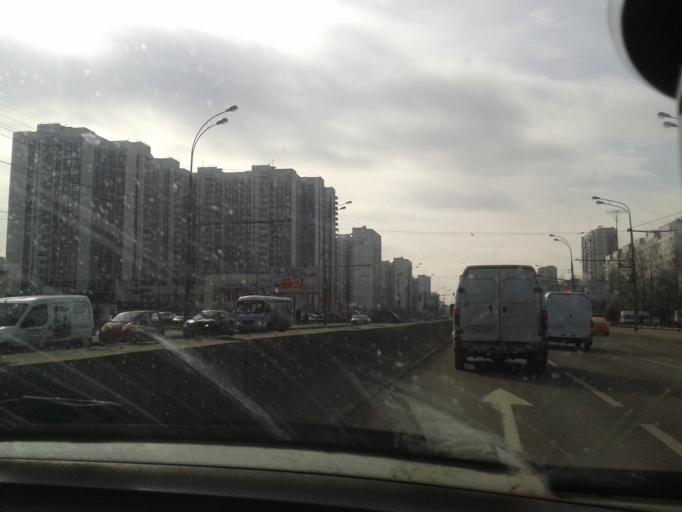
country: RU
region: Moscow
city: Lianozovo
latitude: 55.8997
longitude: 37.5869
